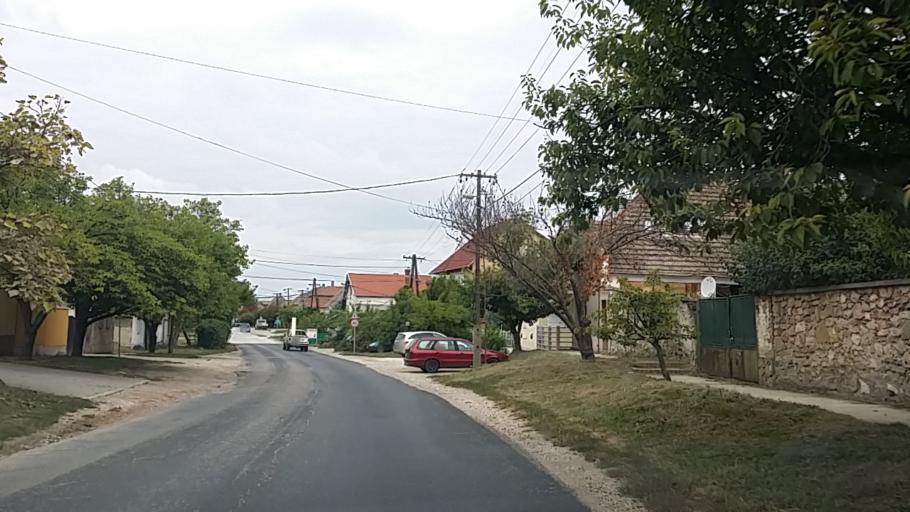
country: HU
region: Komarom-Esztergom
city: Tata
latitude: 47.6455
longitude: 18.3078
